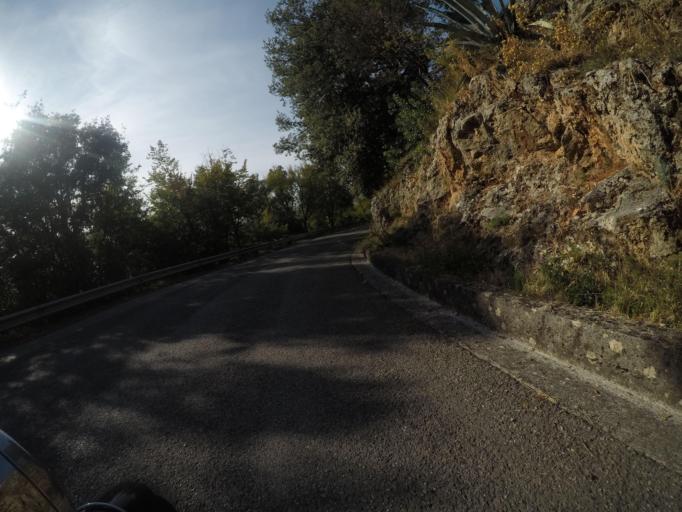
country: IT
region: Tuscany
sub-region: Provincia di Massa-Carrara
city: Massa
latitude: 44.0643
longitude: 10.1218
